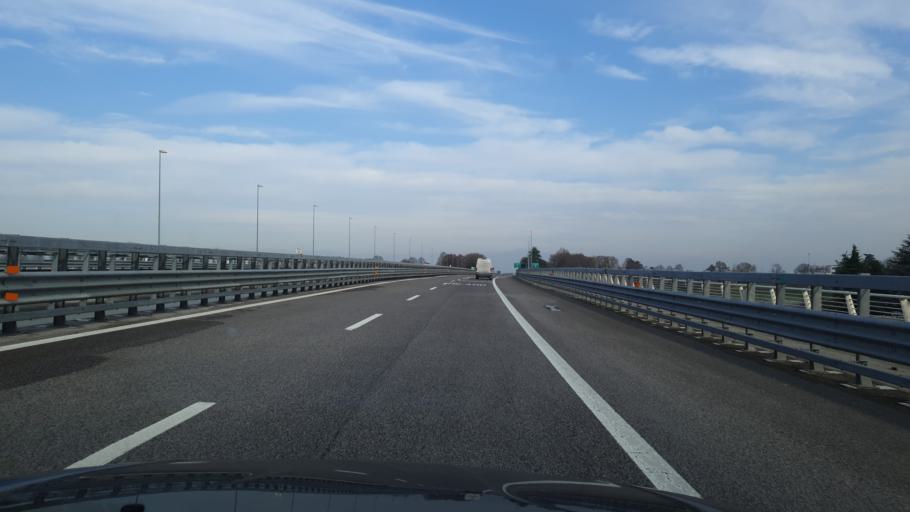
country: IT
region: Veneto
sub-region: Provincia di Vicenza
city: Torri di Quartesolo
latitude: 45.5040
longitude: 11.6164
